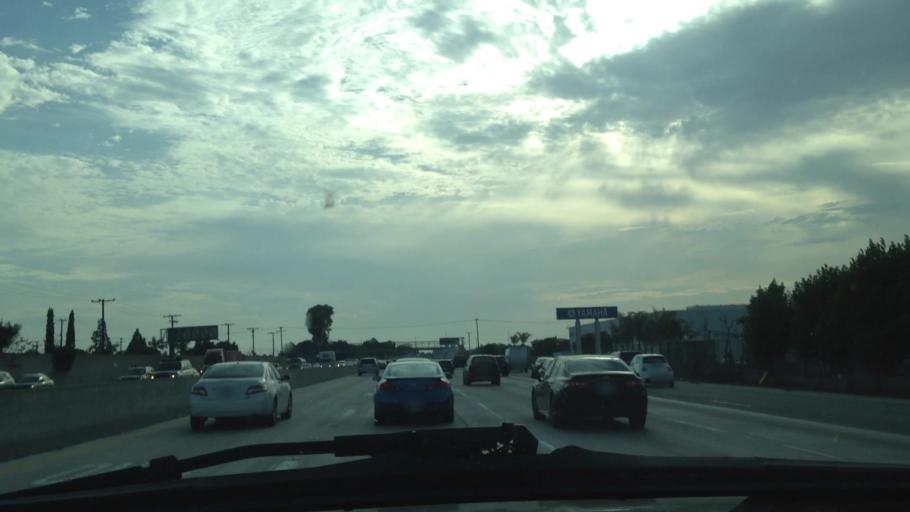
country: US
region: California
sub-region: Orange County
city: Buena Park
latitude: 33.8563
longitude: -118.0174
